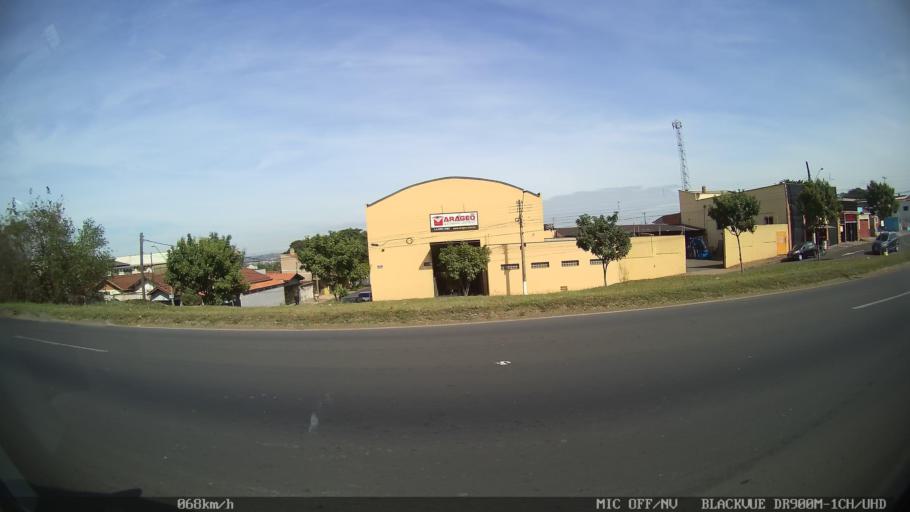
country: BR
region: Sao Paulo
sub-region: Piracicaba
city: Piracicaba
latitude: -22.6971
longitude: -47.6613
